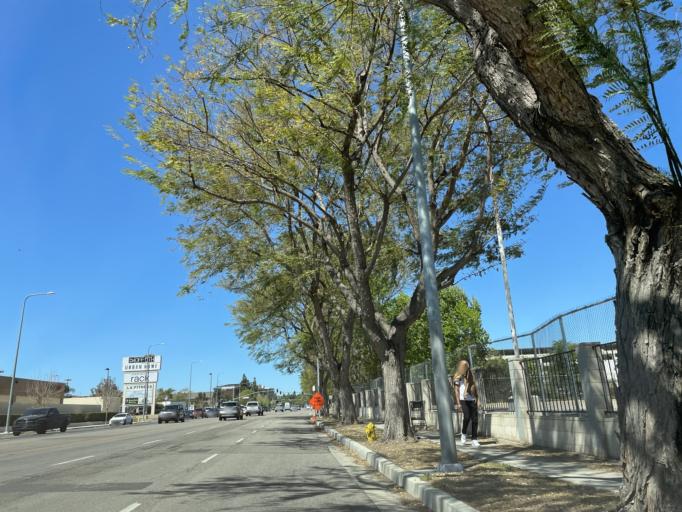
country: US
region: California
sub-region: Los Angeles County
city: Canoga Park
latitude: 34.1883
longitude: -118.5991
